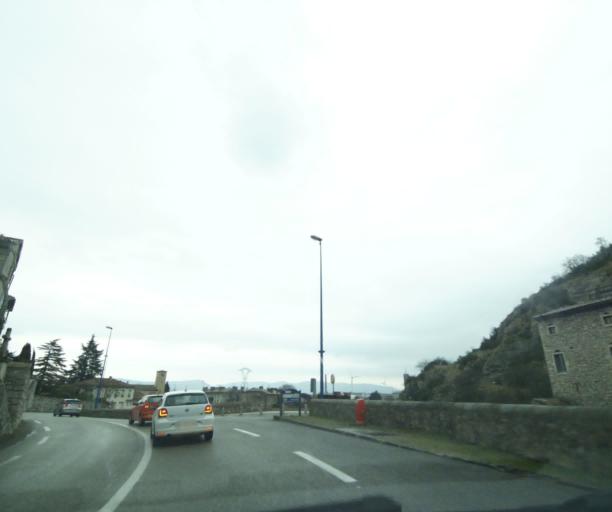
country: FR
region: Rhone-Alpes
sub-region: Departement de l'Ardeche
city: Le Pouzin
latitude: 44.7570
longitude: 4.7458
